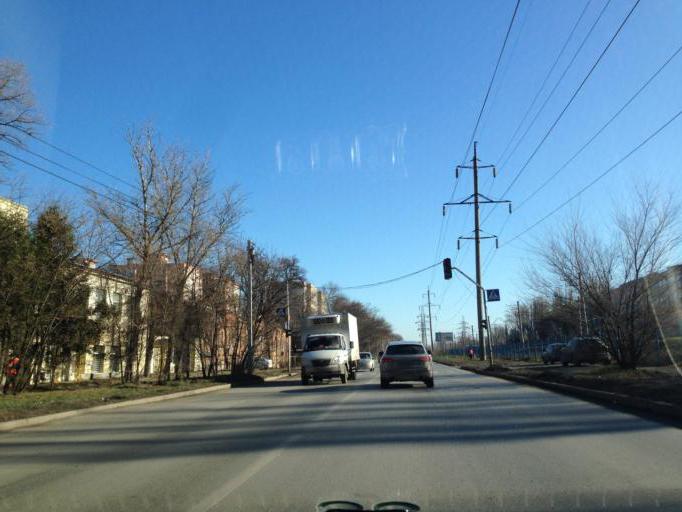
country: RU
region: Rostov
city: Rostov-na-Donu
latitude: 47.2449
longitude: 39.7069
